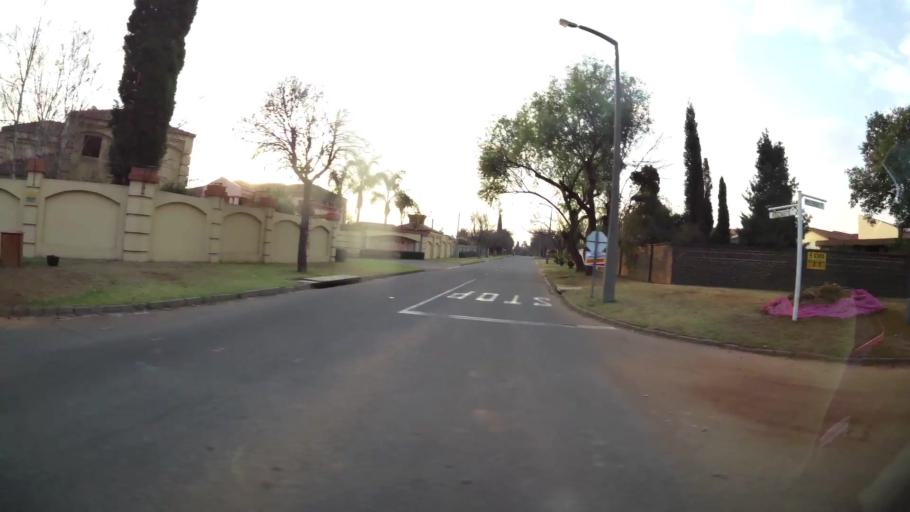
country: ZA
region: Gauteng
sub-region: Ekurhuleni Metropolitan Municipality
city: Benoni
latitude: -26.1685
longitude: 28.3023
